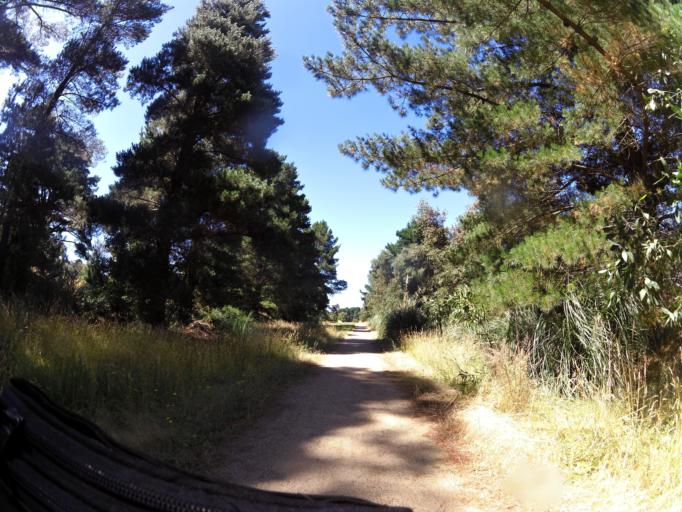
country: AU
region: Victoria
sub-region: Ballarat North
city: Delacombe
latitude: -37.6852
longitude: 143.5662
